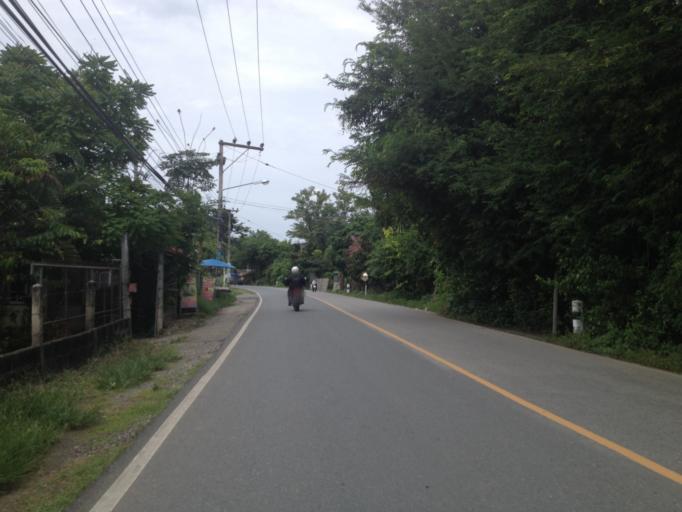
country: TH
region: Chiang Mai
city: Saraphi
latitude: 18.7167
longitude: 98.9861
